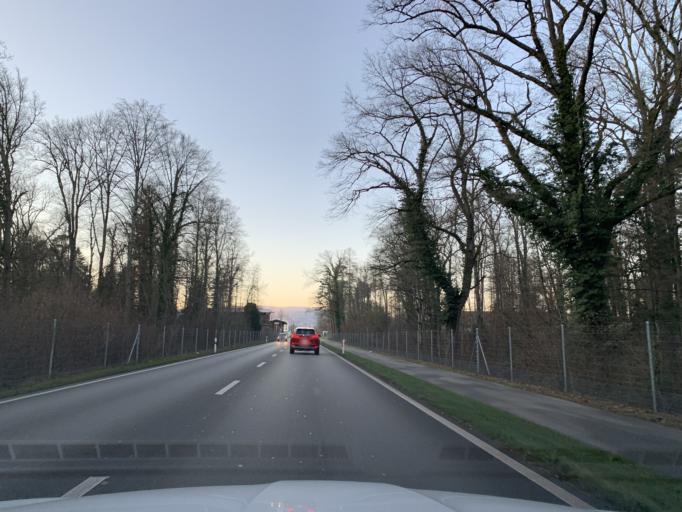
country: CH
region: Zurich
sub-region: Bezirk Dielsdorf
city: Regensdorf
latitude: 47.4344
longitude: 8.4801
